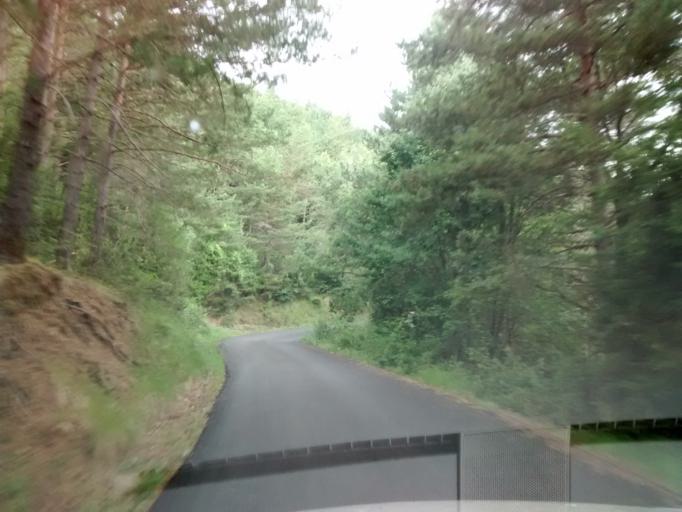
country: ES
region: Aragon
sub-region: Provincia de Huesca
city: Puertolas
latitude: 42.5609
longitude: 0.1410
